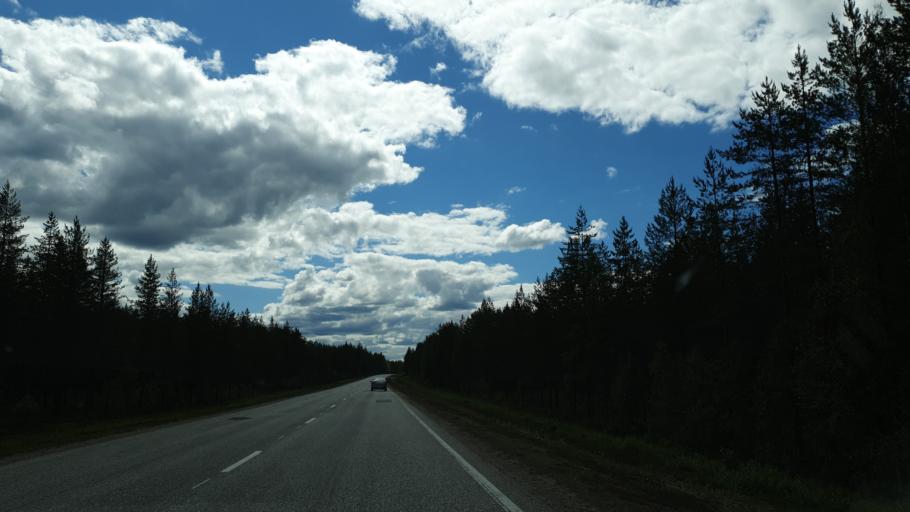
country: FI
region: North Karelia
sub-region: Pielisen Karjala
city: Valtimo
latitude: 63.4564
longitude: 28.7985
